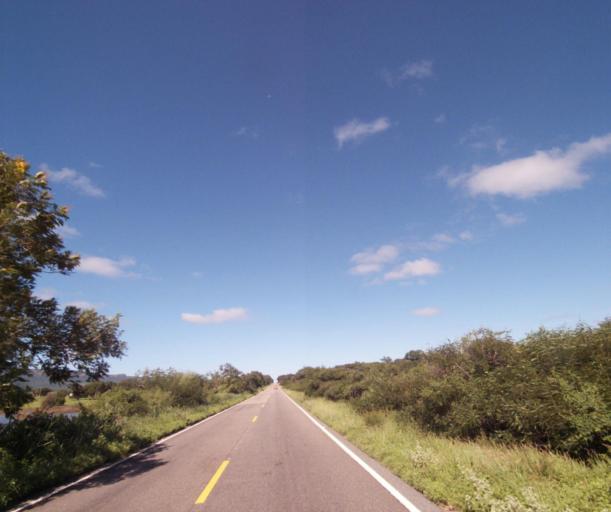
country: BR
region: Bahia
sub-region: Palmas De Monte Alto
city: Palmas de Monte Alto
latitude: -14.2425
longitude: -43.0750
